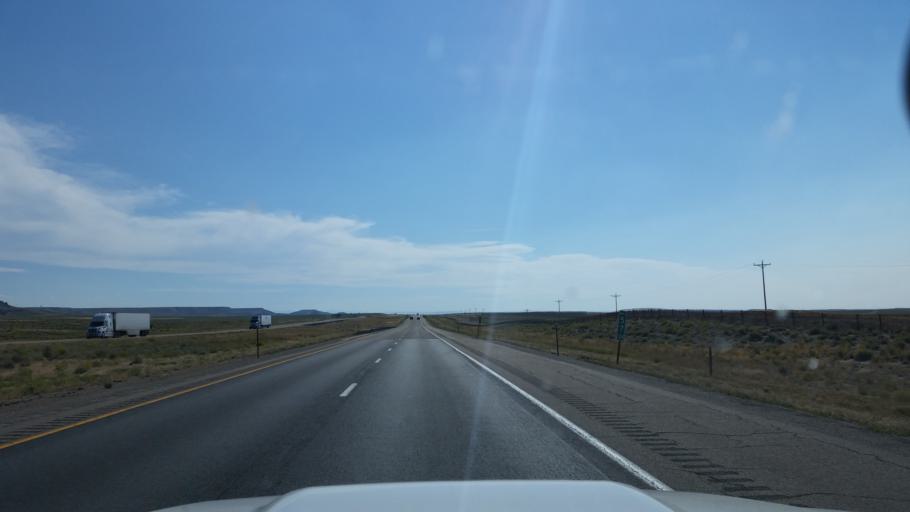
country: US
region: Wyoming
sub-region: Uinta County
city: Lyman
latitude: 41.4650
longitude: -110.0488
